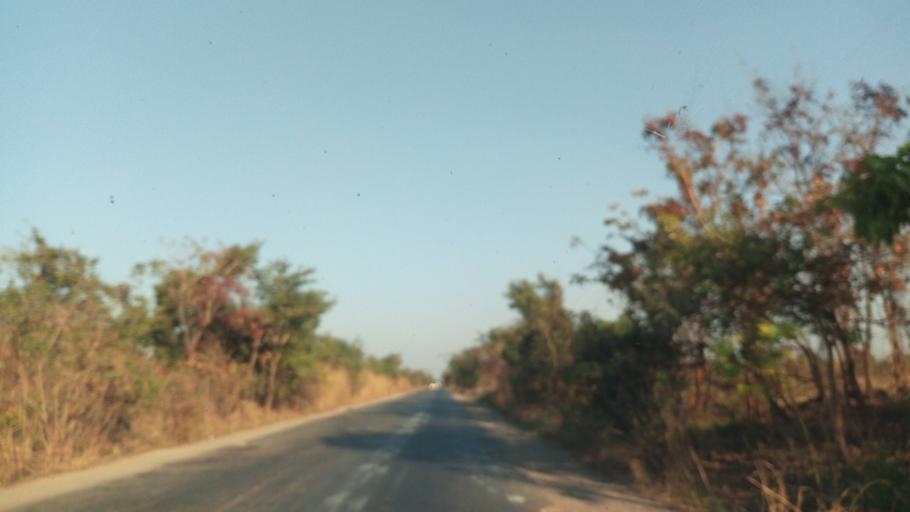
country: CD
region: Katanga
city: Likasi
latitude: -11.1163
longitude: 27.0278
